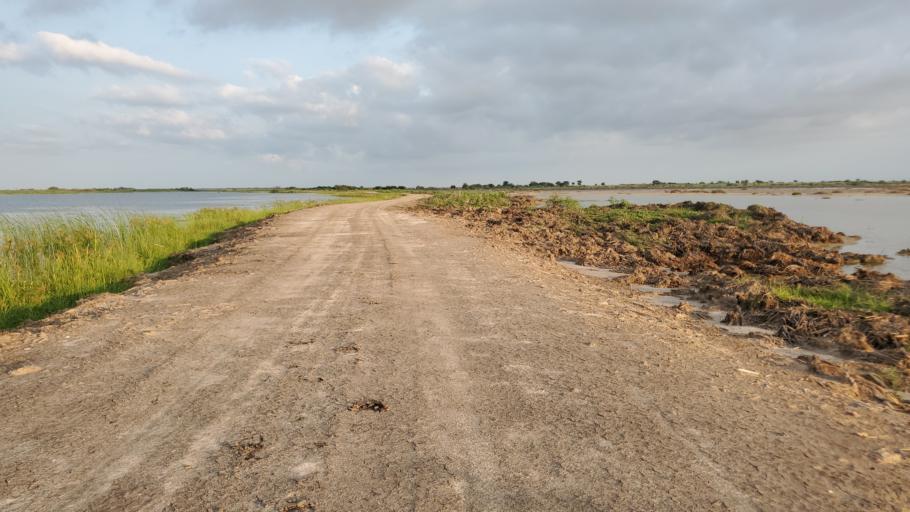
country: SN
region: Saint-Louis
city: Saint-Louis
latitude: 16.0208
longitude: -16.4074
